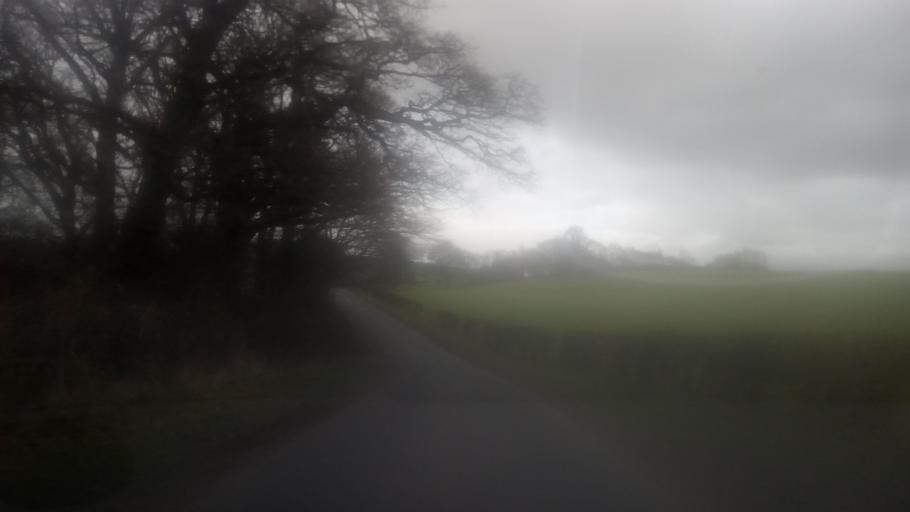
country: GB
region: Scotland
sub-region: The Scottish Borders
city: Jedburgh
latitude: 55.4879
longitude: -2.4806
